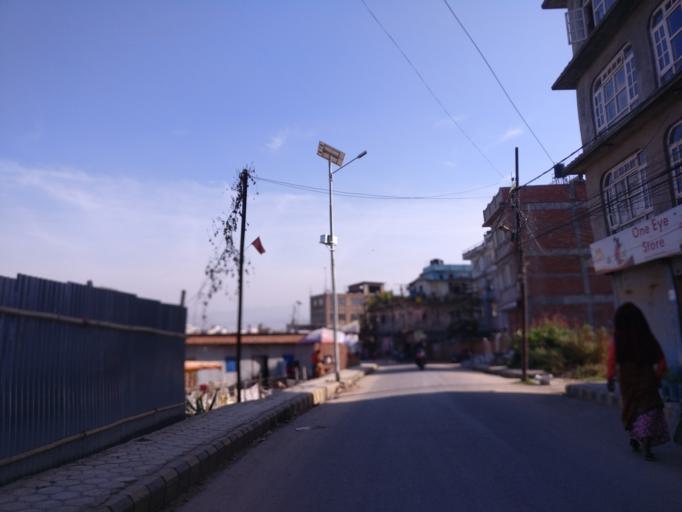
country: NP
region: Central Region
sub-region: Bagmati Zone
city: Patan
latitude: 27.6744
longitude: 85.3352
